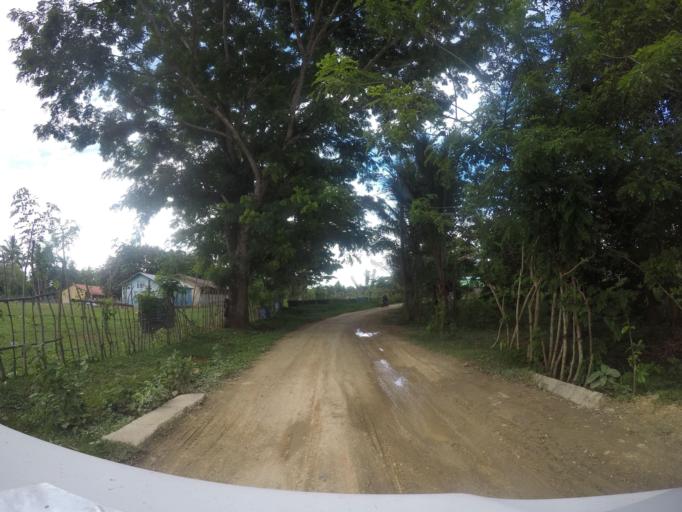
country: TL
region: Lautem
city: Lospalos
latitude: -8.5045
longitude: 126.9909
